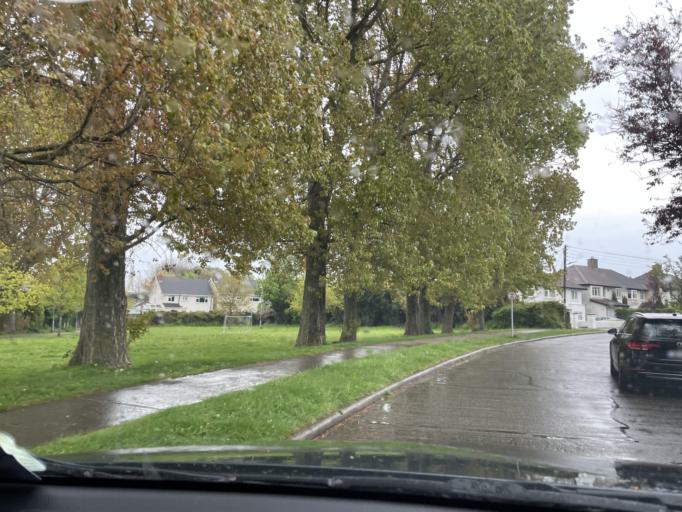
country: IE
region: Leinster
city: Dundrum
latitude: 53.2932
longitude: -6.2549
